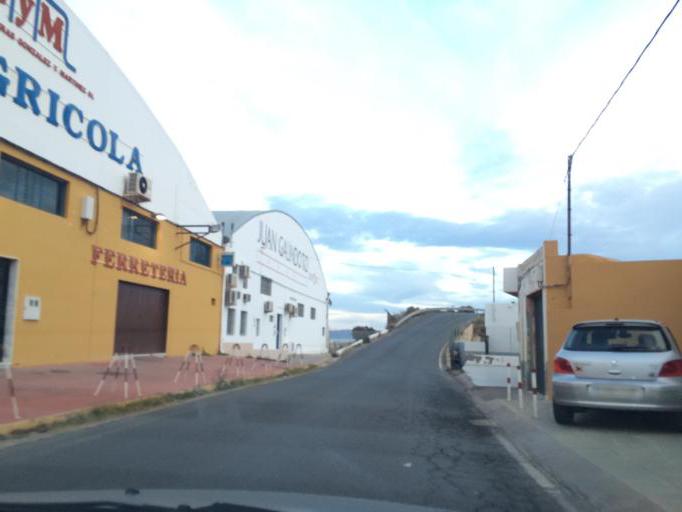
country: ES
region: Andalusia
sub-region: Provincia de Almeria
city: Viator
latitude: 36.8445
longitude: -2.4000
